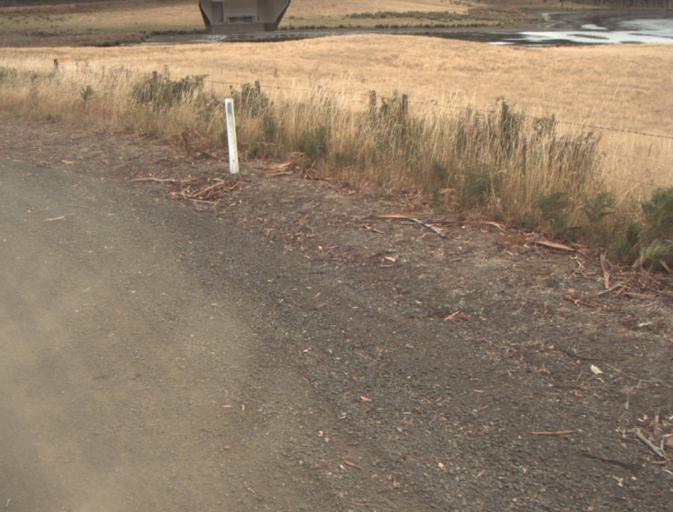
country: AU
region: Tasmania
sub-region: Northern Midlands
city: Evandale
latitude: -41.4590
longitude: 147.4604
